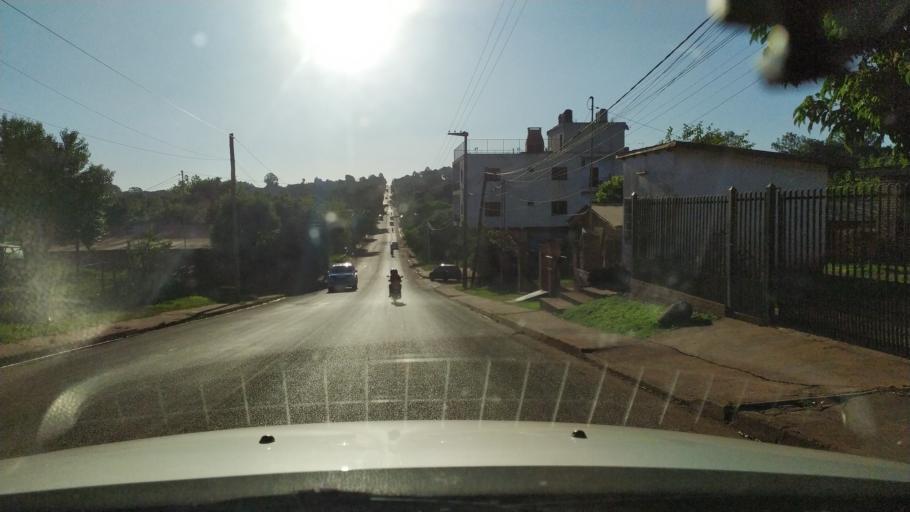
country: AR
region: Misiones
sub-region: Departamento de Eldorado
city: Eldorado
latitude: -26.4145
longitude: -54.6210
